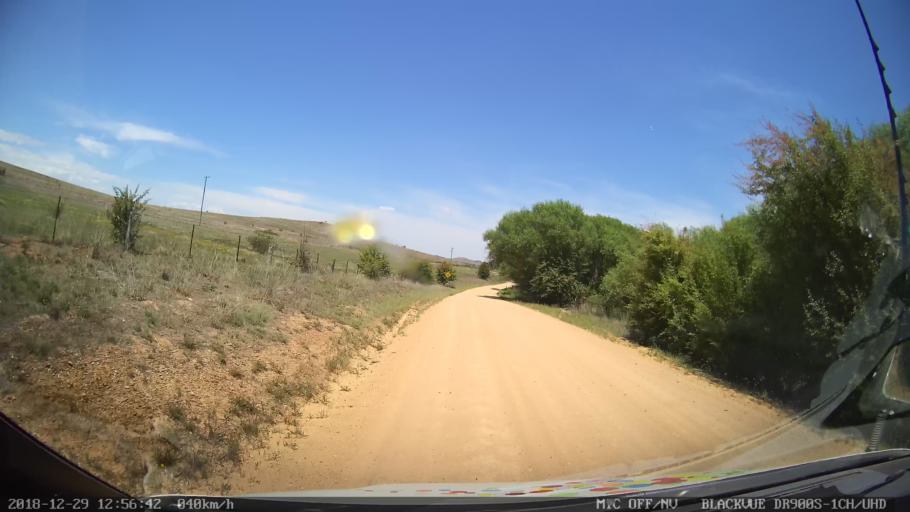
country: AU
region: Australian Capital Territory
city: Macarthur
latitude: -35.7031
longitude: 149.1809
